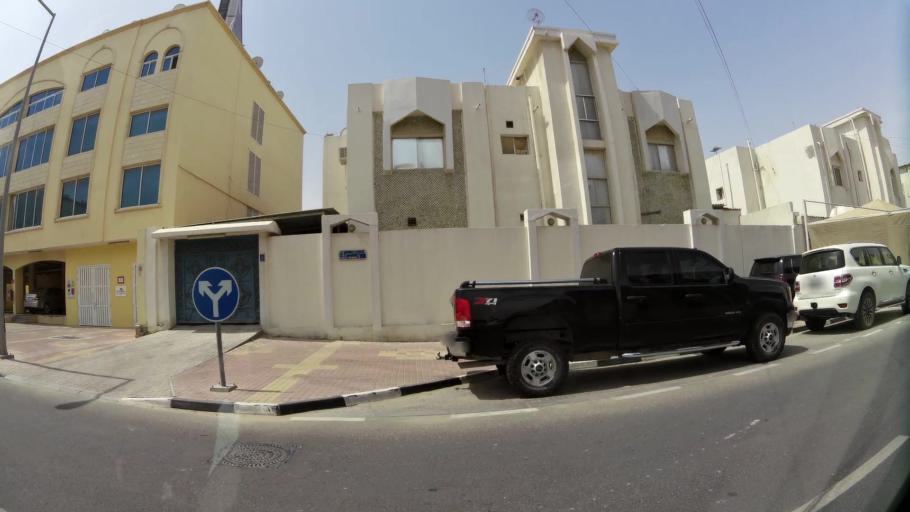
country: QA
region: Baladiyat ar Rayyan
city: Ar Rayyan
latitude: 25.3158
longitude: 51.4716
